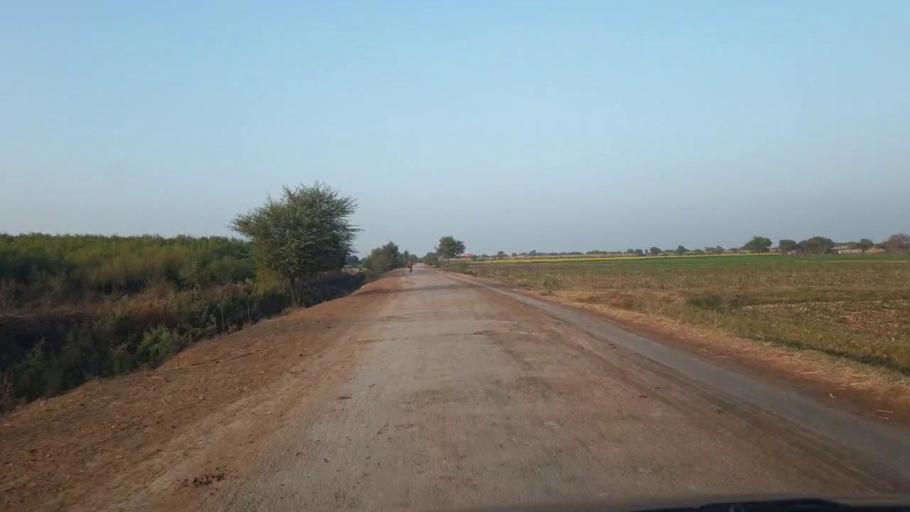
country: PK
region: Sindh
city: Berani
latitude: 25.8312
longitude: 68.7442
